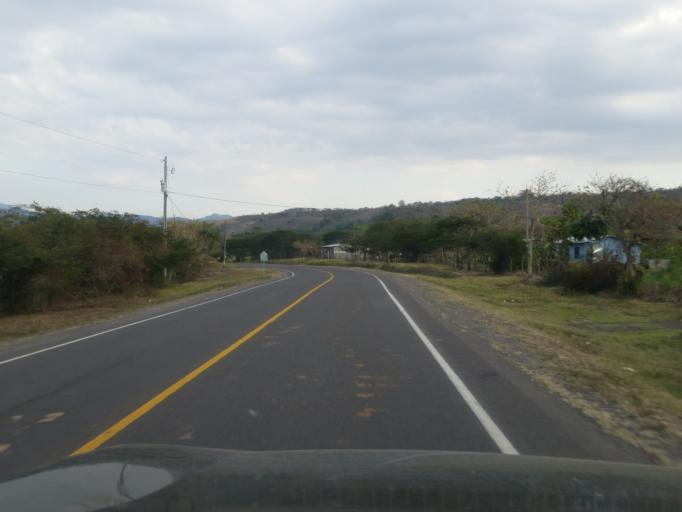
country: NI
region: Jinotega
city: Jinotega
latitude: 13.1522
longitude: -86.0586
